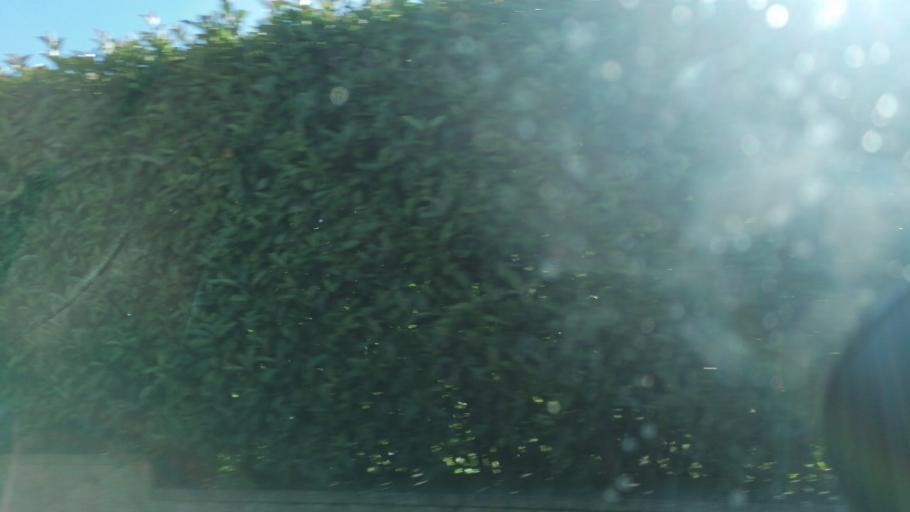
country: PT
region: Porto
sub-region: Santo Tirso
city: Sao Miguel do Couto
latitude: 41.3095
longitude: -8.4714
